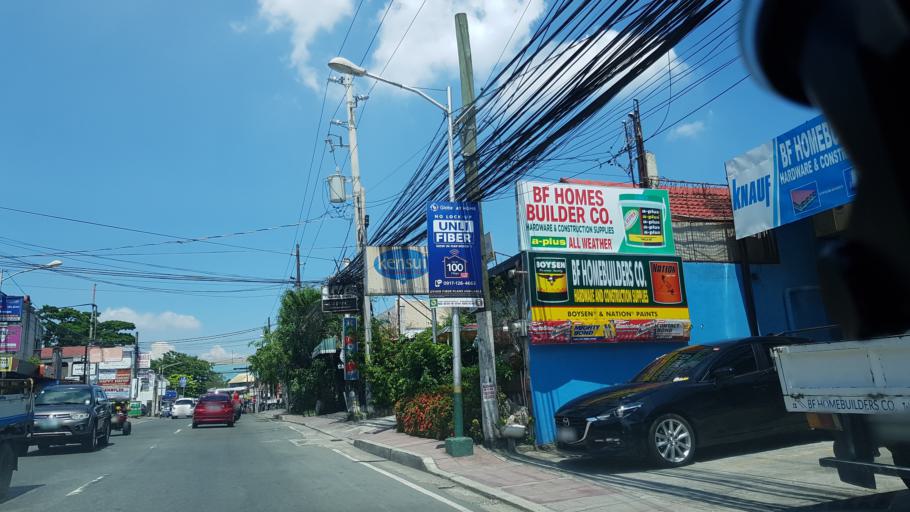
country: PH
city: Sambayanihan People's Village
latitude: 14.4538
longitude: 121.0304
